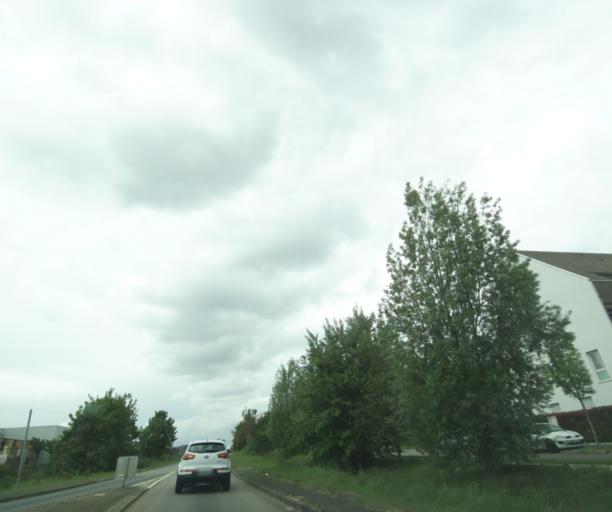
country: FR
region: Ile-de-France
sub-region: Departement des Yvelines
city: Ecquevilly
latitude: 48.9498
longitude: 1.9281
